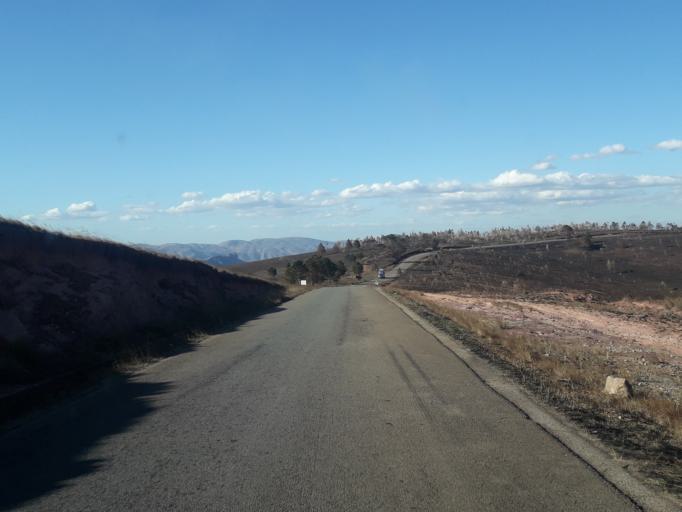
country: MG
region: Analamanga
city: Ankazobe
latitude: -17.8704
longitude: 47.0547
